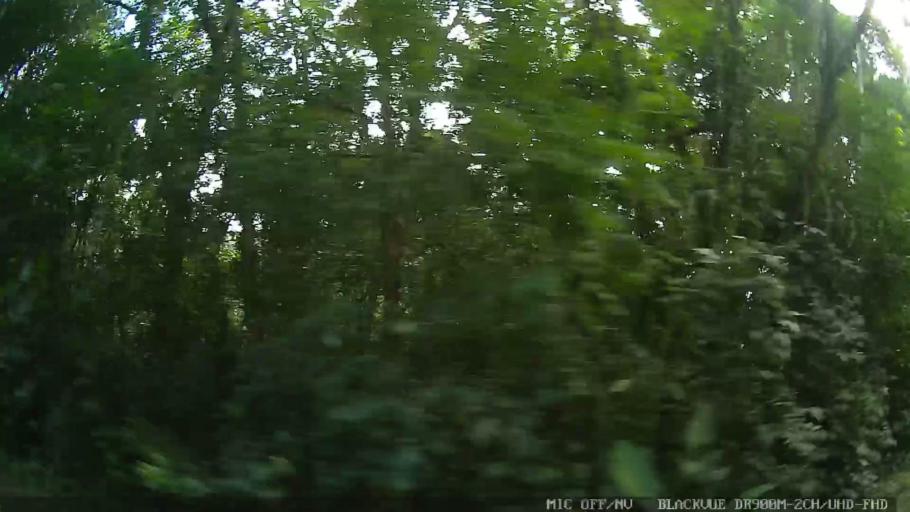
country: BR
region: Sao Paulo
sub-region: Iguape
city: Iguape
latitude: -24.6859
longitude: -47.5017
